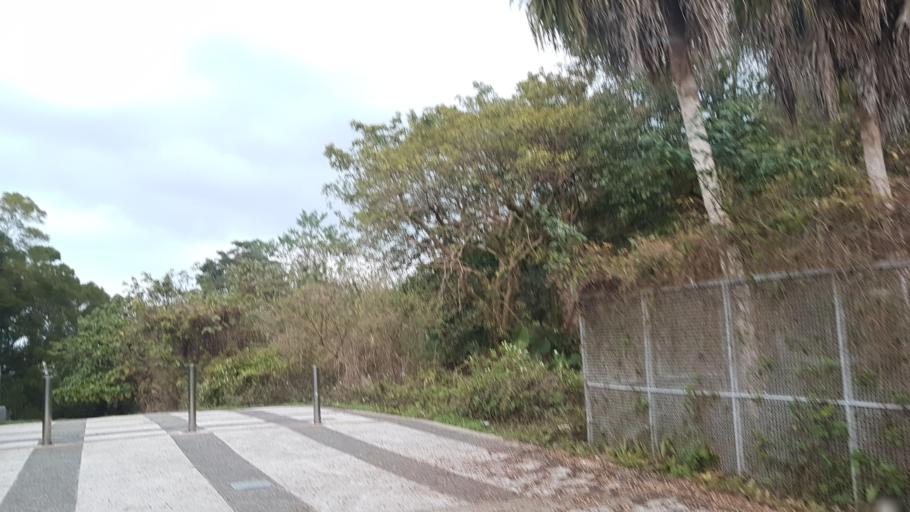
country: TW
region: Taiwan
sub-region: Chiayi
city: Jiayi Shi
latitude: 23.3284
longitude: 120.4868
